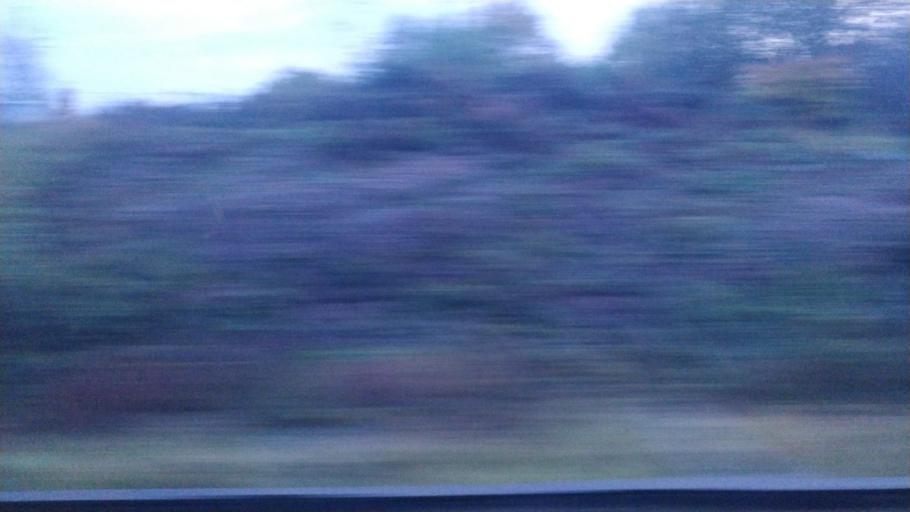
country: GB
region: England
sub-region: Borough of Wigan
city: Atherton
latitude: 53.5378
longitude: -2.5072
